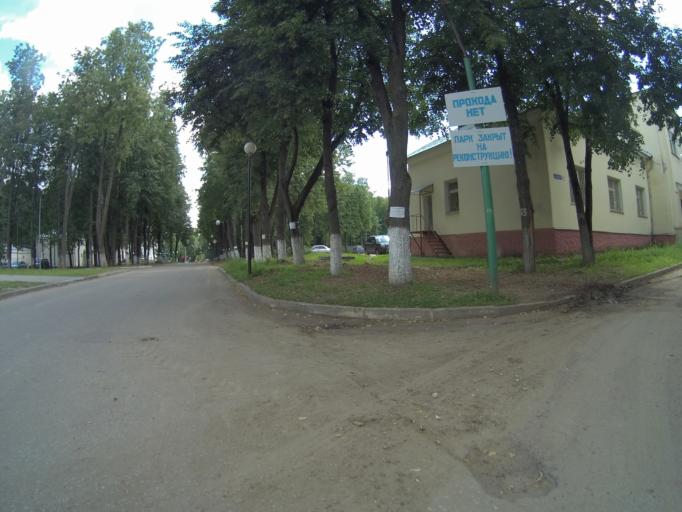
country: RU
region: Vladimir
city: Vladimir
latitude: 56.1434
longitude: 40.4132
